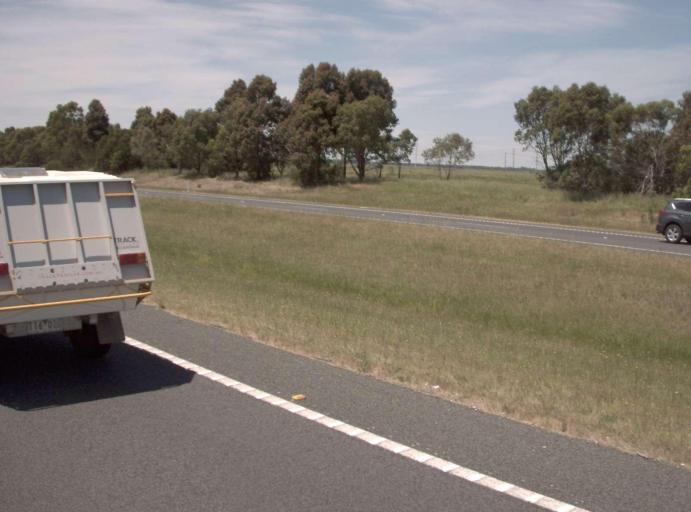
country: AU
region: Victoria
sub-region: Latrobe
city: Morwell
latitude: -38.2366
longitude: 146.4518
